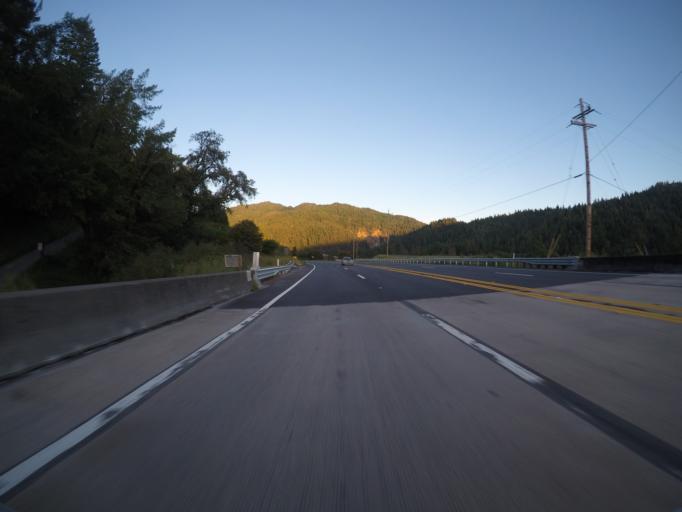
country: US
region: California
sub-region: Humboldt County
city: Redway
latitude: 39.9345
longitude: -123.7704
